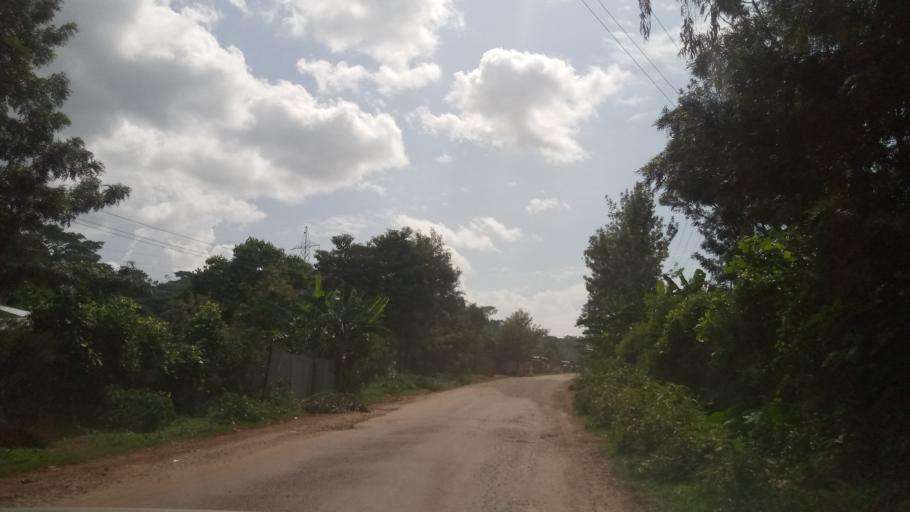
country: ET
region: Oromiya
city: Agaro
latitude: 7.9206
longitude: 36.5205
